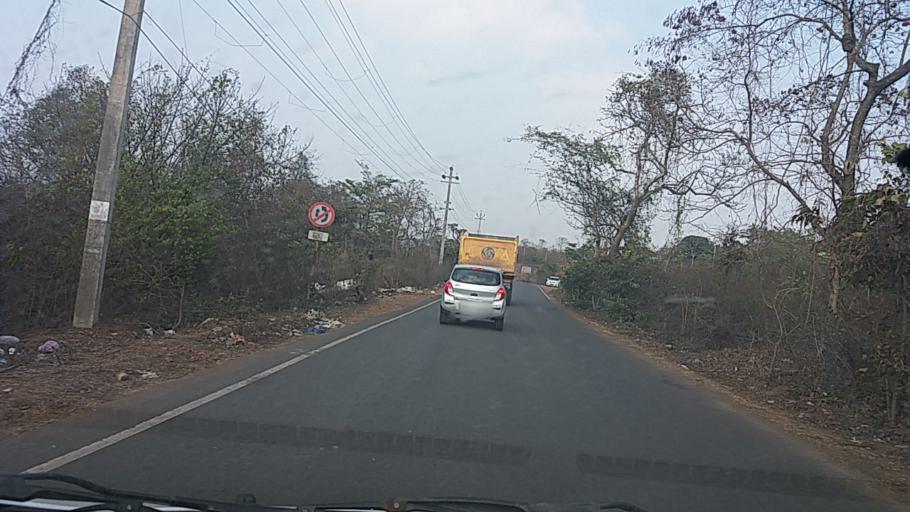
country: IN
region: Goa
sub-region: North Goa
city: Goa Velha
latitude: 15.4882
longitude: 73.9042
